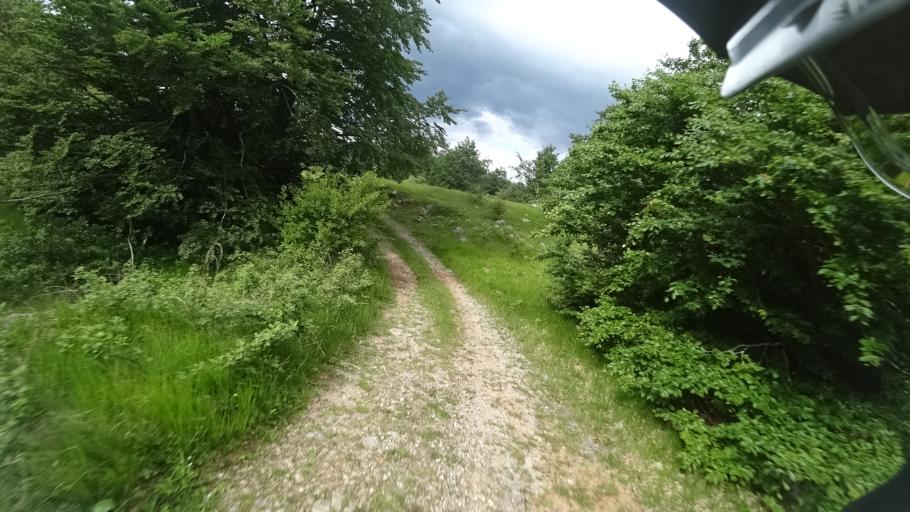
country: HR
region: Zadarska
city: Obrovac
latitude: 44.2714
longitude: 15.7400
